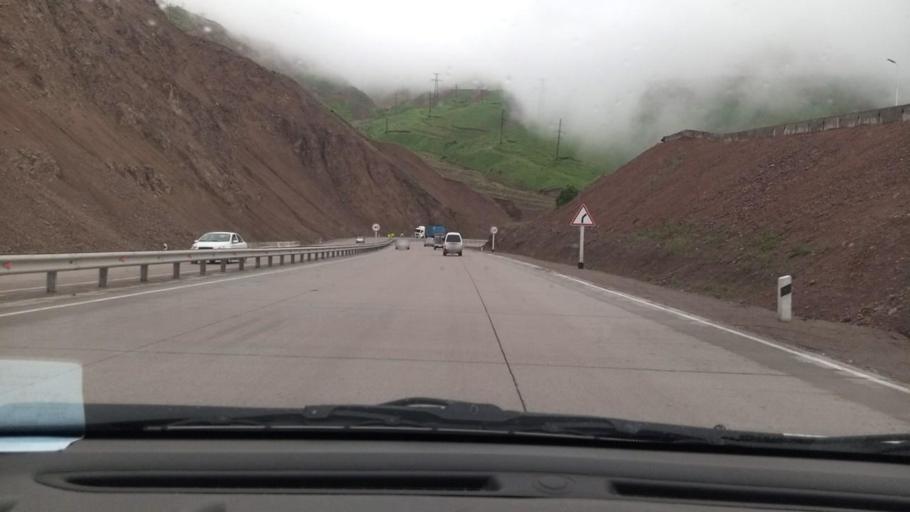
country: UZ
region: Toshkent
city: Angren
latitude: 41.1057
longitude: 70.5067
